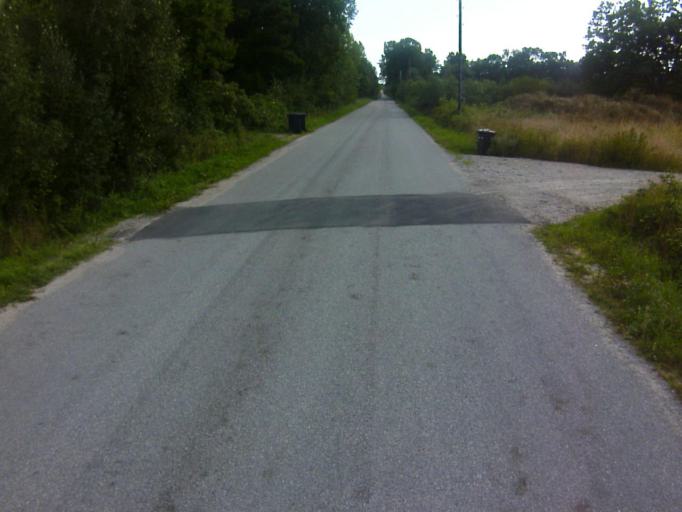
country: SE
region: Blekinge
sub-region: Solvesborgs Kommun
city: Soelvesborg
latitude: 56.0093
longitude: 14.6749
